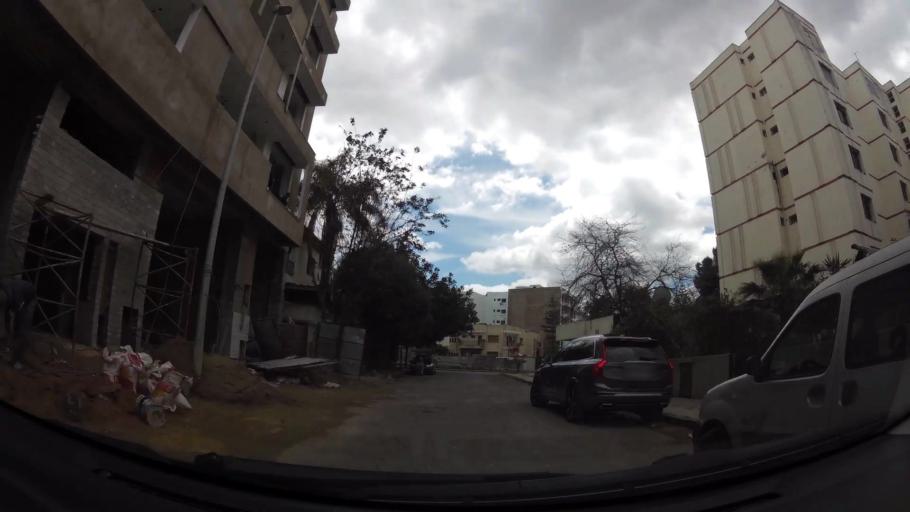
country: MA
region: Grand Casablanca
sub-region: Casablanca
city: Casablanca
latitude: 33.5787
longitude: -7.6494
